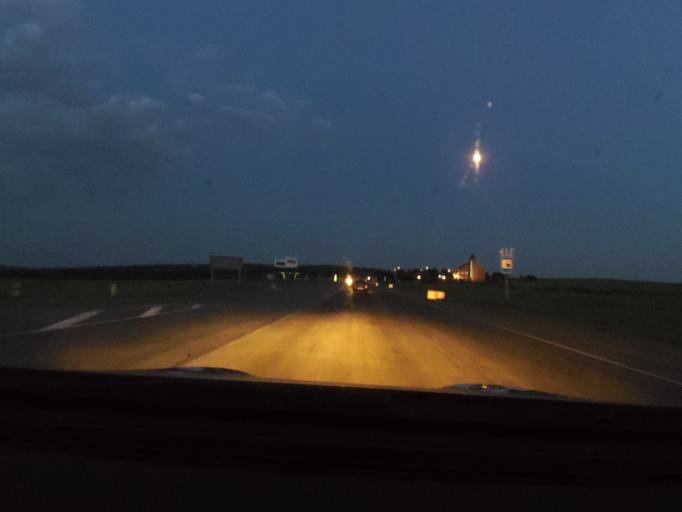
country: RU
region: Bashkortostan
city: Duvan
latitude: 55.9184
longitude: 58.2087
